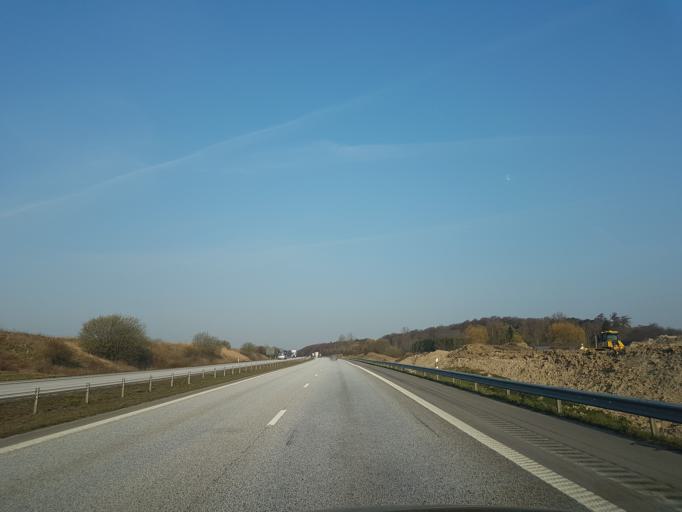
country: SE
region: Skane
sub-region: Svedala Kommun
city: Svedala
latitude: 55.5228
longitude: 13.2300
